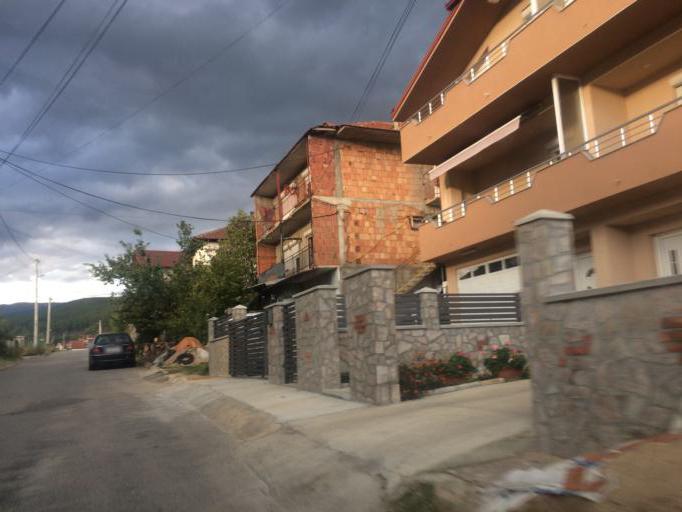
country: MK
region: Makedonska Kamenica
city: Makedonska Kamenica
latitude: 42.0173
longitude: 22.5918
